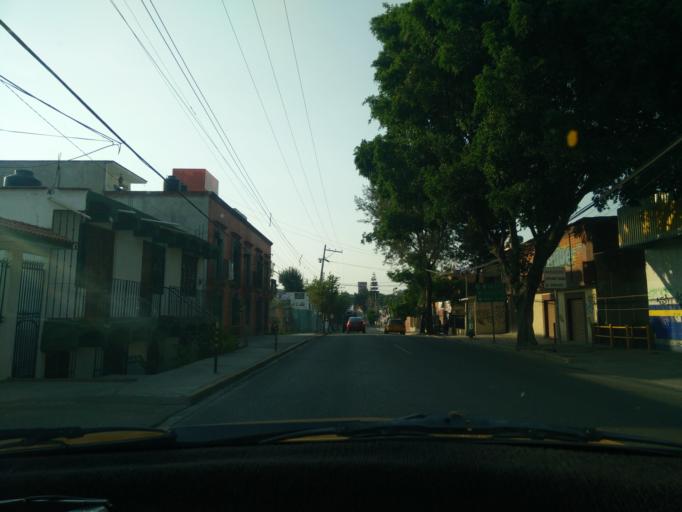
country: MX
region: Oaxaca
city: Oaxaca de Juarez
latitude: 17.0769
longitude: -96.7401
